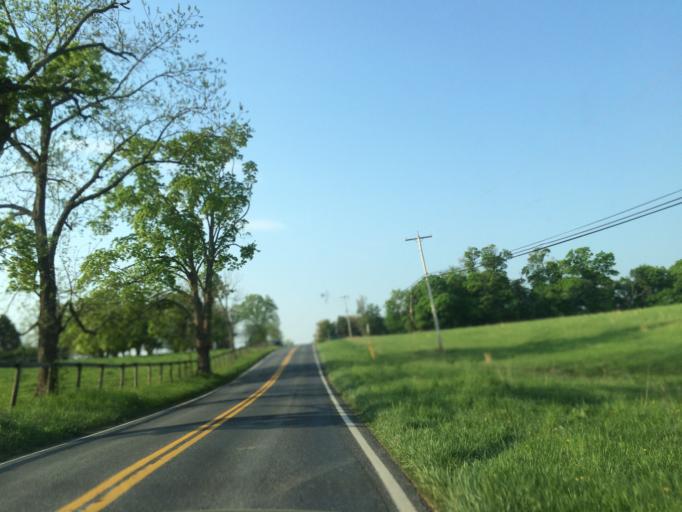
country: US
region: Maryland
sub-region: Carroll County
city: Sykesville
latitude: 39.2958
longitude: -76.9908
